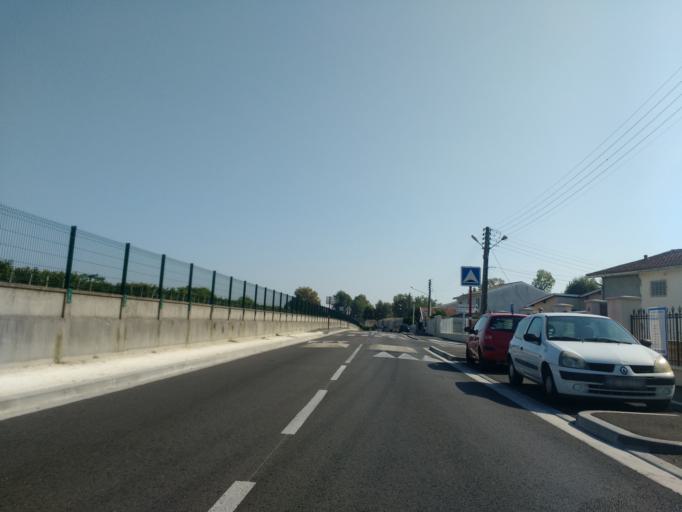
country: FR
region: Aquitaine
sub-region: Departement de la Gironde
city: Talence
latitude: 44.8083
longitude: -0.6142
